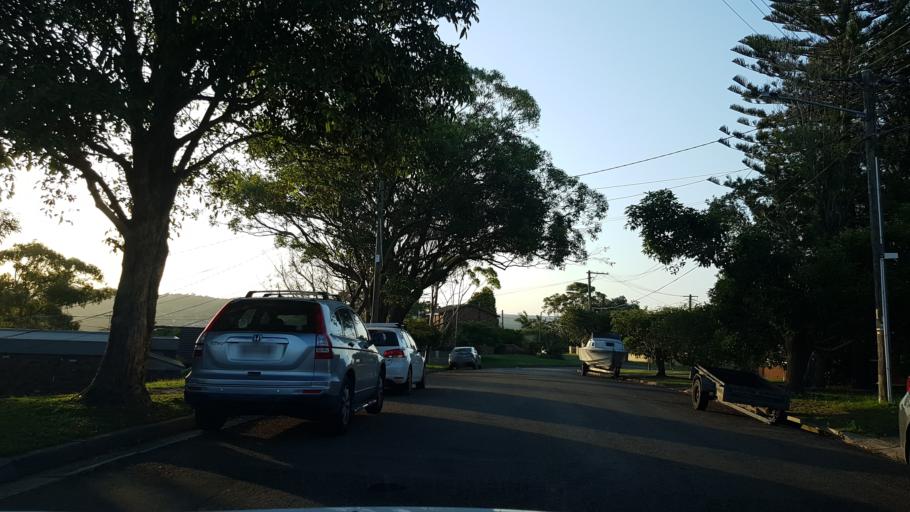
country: AU
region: New South Wales
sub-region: Warringah
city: Narrabeen
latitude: -33.7292
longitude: 151.2838
